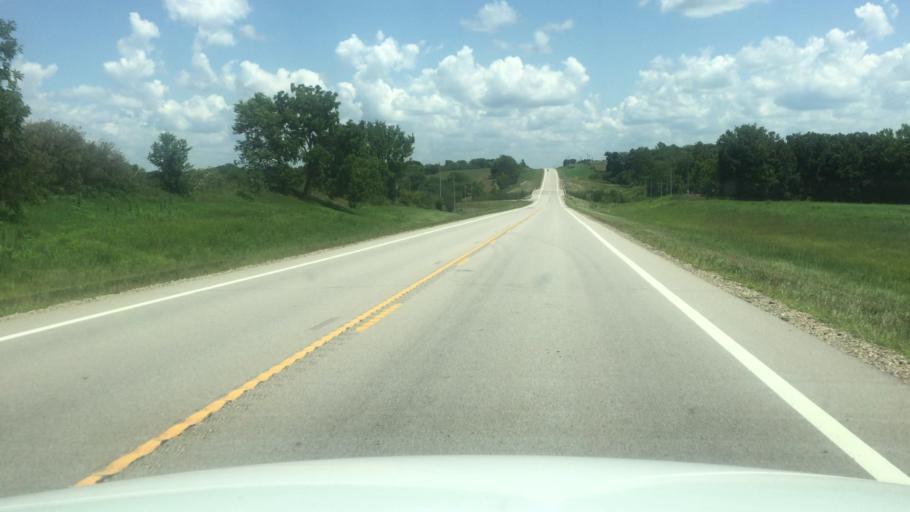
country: US
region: Kansas
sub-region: Brown County
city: Horton
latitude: 39.6672
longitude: -95.4773
